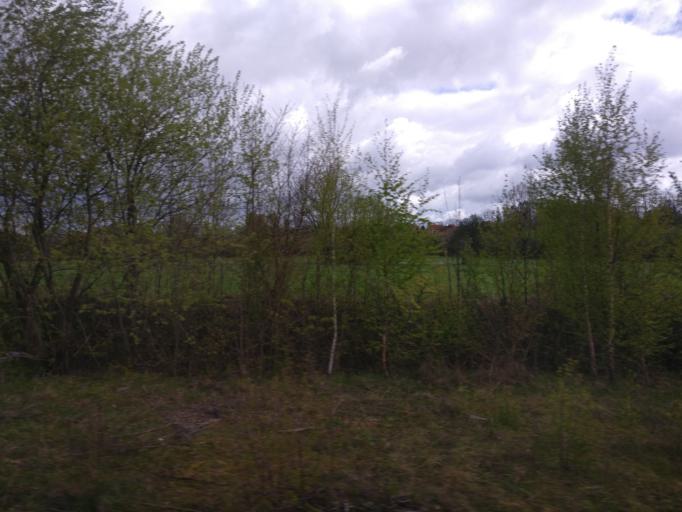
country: DE
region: Saxony-Anhalt
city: Darlingerode
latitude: 51.8536
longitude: 10.7276
